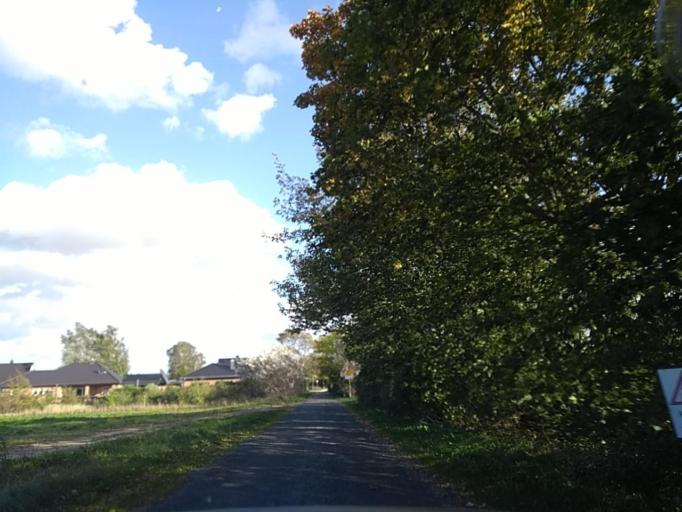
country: DE
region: Mecklenburg-Vorpommern
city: Ostseebad Dierhagen
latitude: 54.2324
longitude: 12.3840
